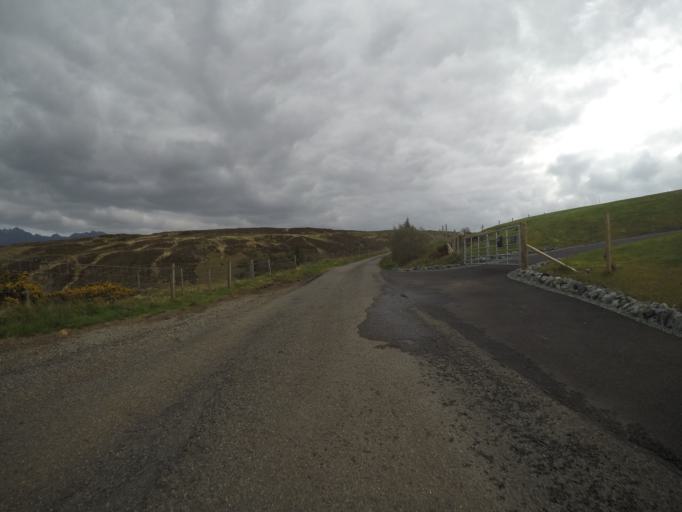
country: GB
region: Scotland
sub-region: Highland
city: Isle of Skye
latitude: 57.2975
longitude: -6.3579
